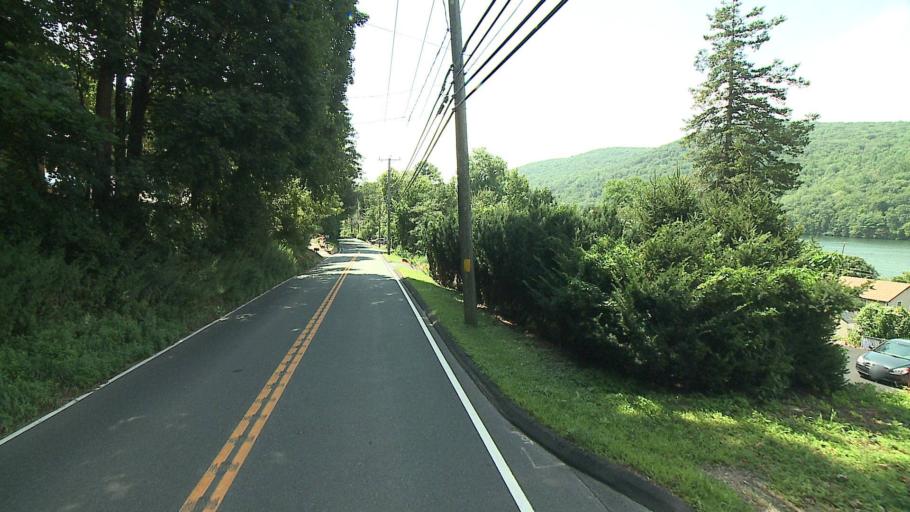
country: US
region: Connecticut
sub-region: Fairfield County
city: Sherman
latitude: 41.5245
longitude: -73.4804
